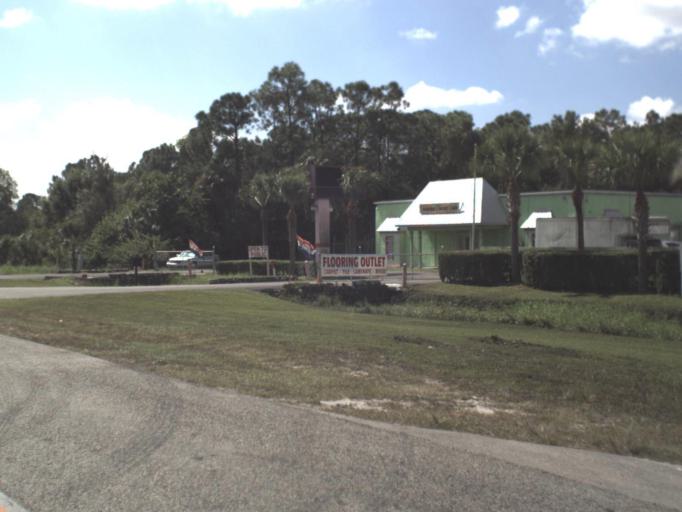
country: US
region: Florida
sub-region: Lee County
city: Suncoast Estates
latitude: 26.7299
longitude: -81.9092
